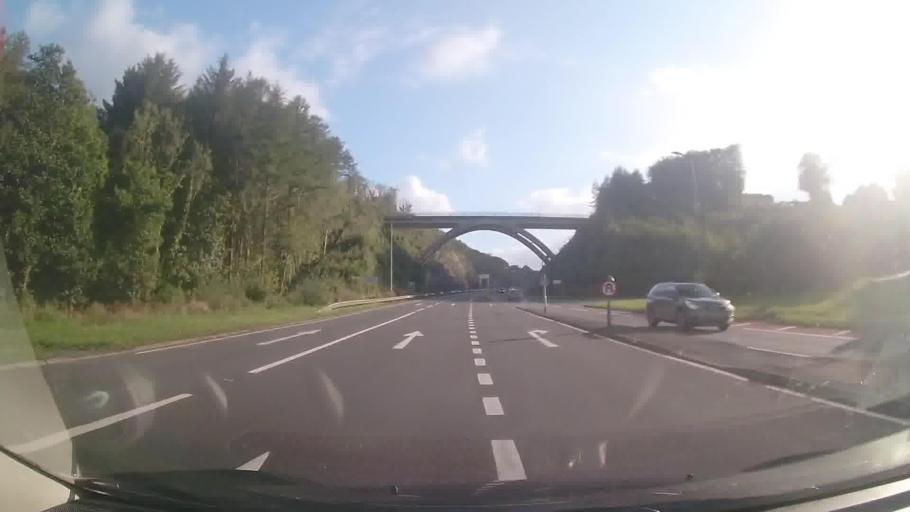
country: GB
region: Wales
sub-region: Pembrokeshire
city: Kilgetty
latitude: 51.7348
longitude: -4.7047
